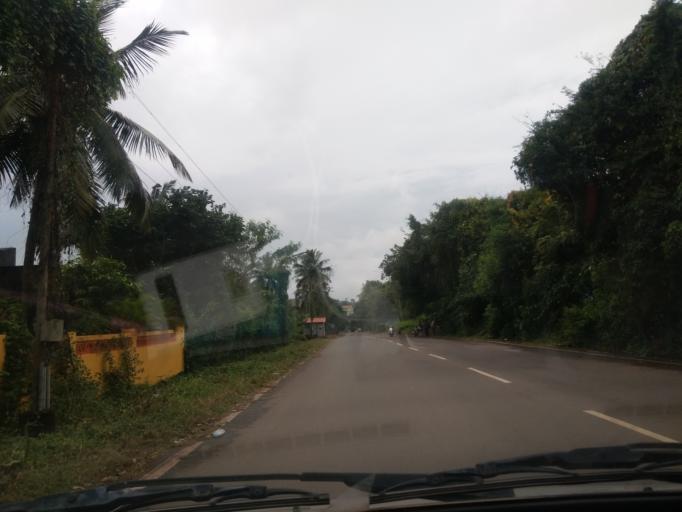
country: IN
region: Goa
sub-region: South Goa
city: Raia
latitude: 15.2913
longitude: 73.9851
